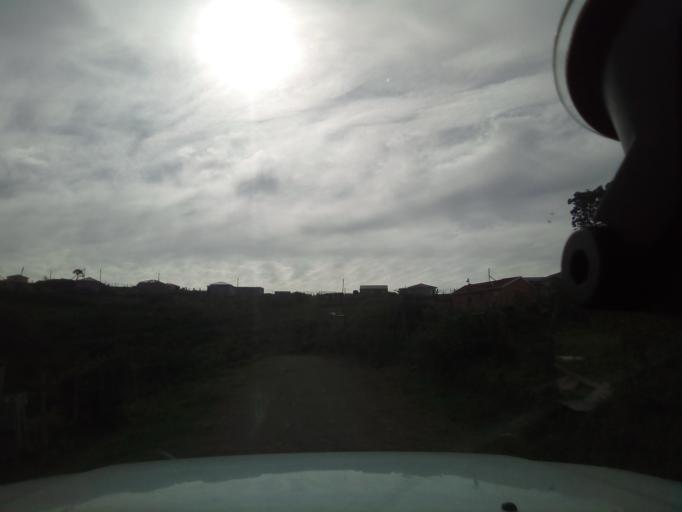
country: ZA
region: Eastern Cape
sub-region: Buffalo City Metropolitan Municipality
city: East London
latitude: -32.7960
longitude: 27.9671
